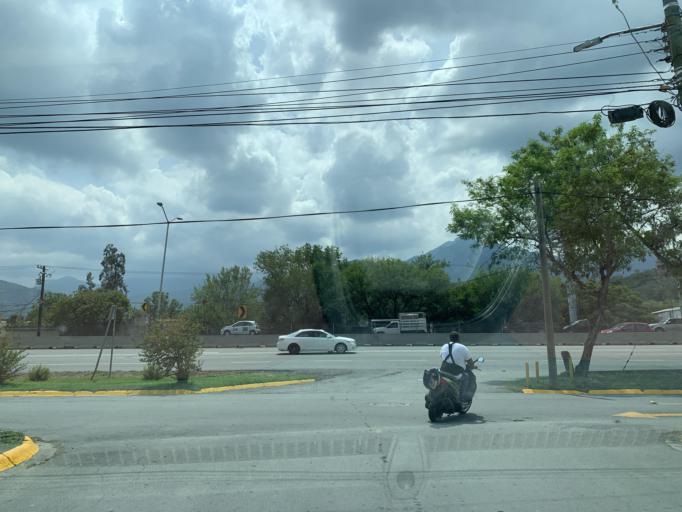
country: MX
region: Nuevo Leon
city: Santiago
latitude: 25.4003
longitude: -100.1309
